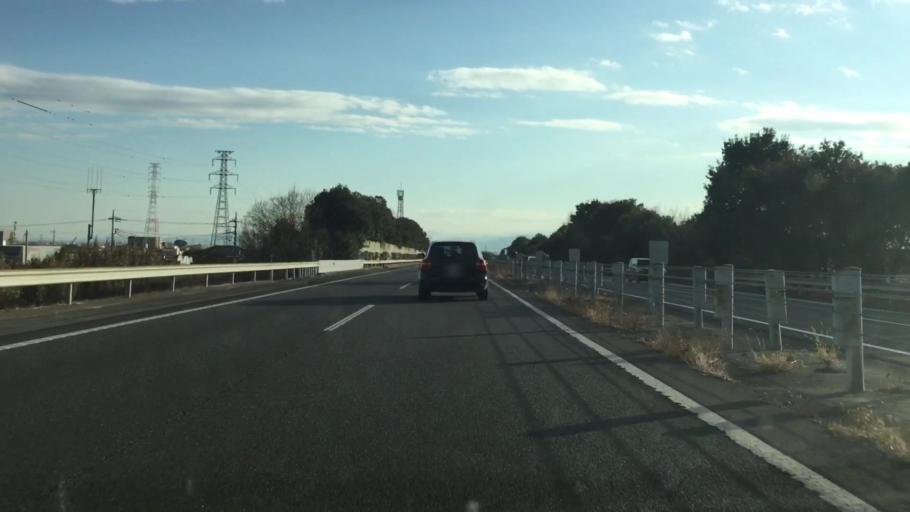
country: JP
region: Gunma
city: Kanekomachi
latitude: 36.3998
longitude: 139.0248
